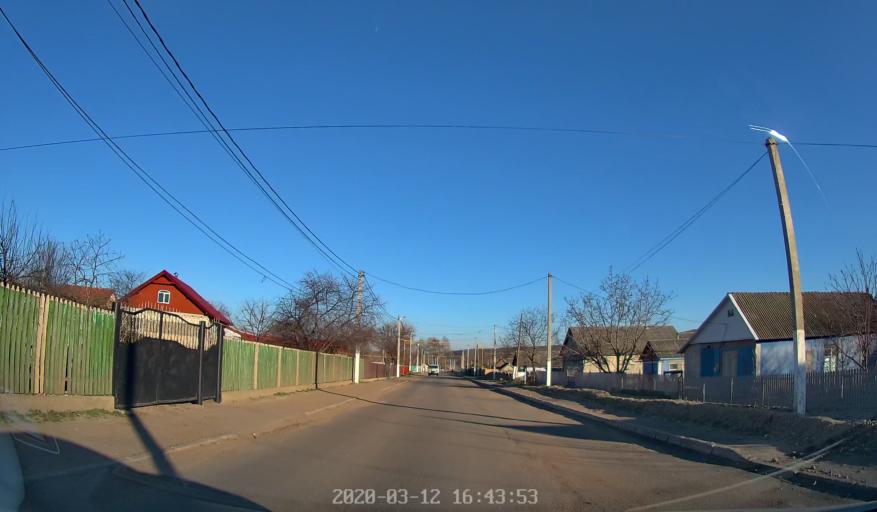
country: MD
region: Anenii Noi
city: Anenii Noi
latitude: 46.8186
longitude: 29.1462
